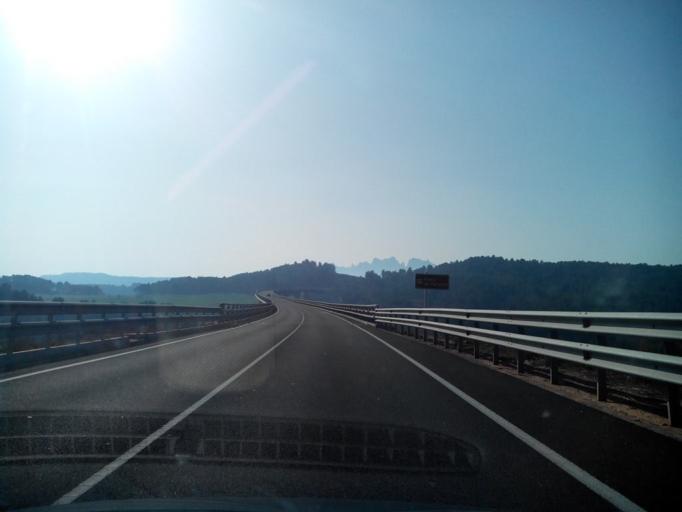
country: ES
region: Catalonia
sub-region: Provincia de Barcelona
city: Sant Joan de Vilatorrada
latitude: 41.7221
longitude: 1.7818
